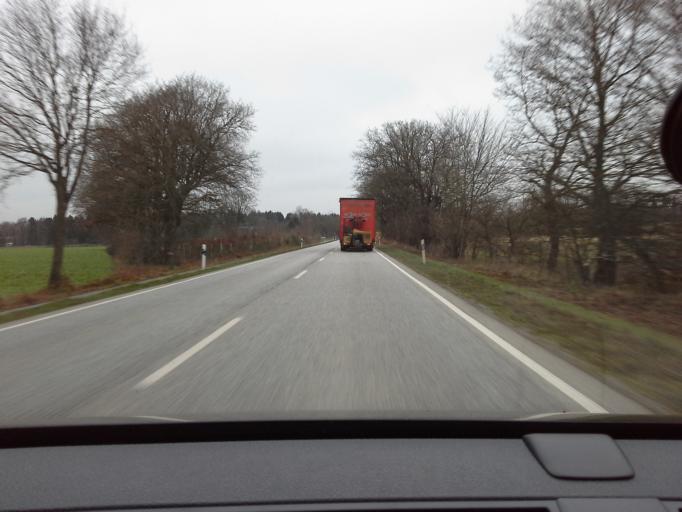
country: DE
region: Schleswig-Holstein
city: Lentfohrden
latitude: 53.8600
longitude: 9.8886
